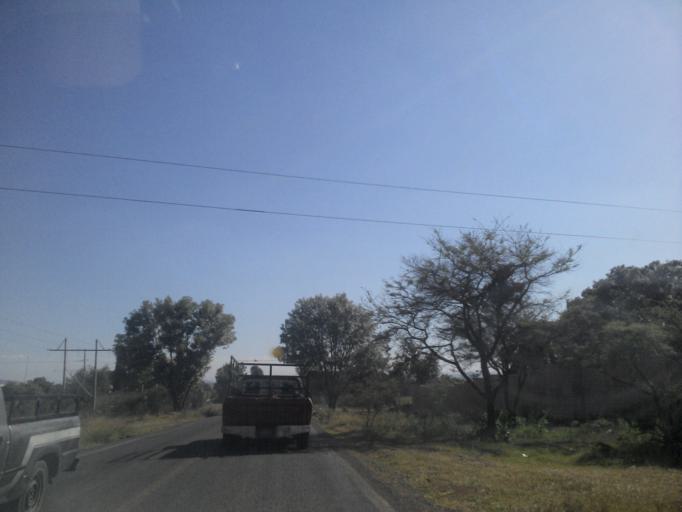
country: MX
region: Jalisco
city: Arandas
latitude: 20.7382
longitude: -102.3179
